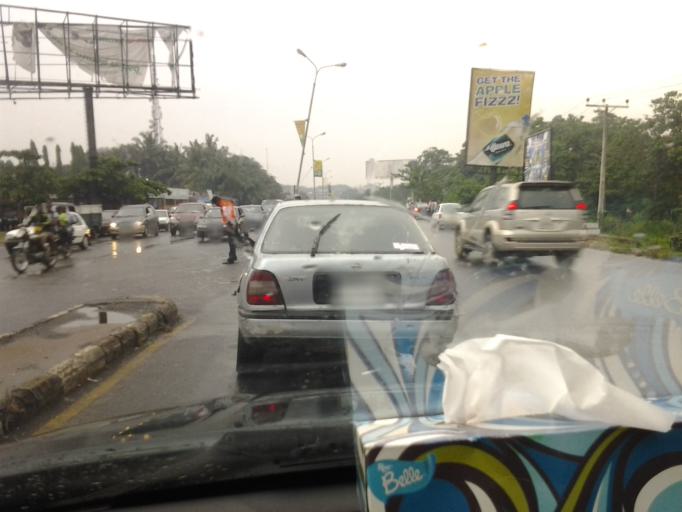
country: NG
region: Oyo
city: Ibadan
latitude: 7.4396
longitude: 3.9070
